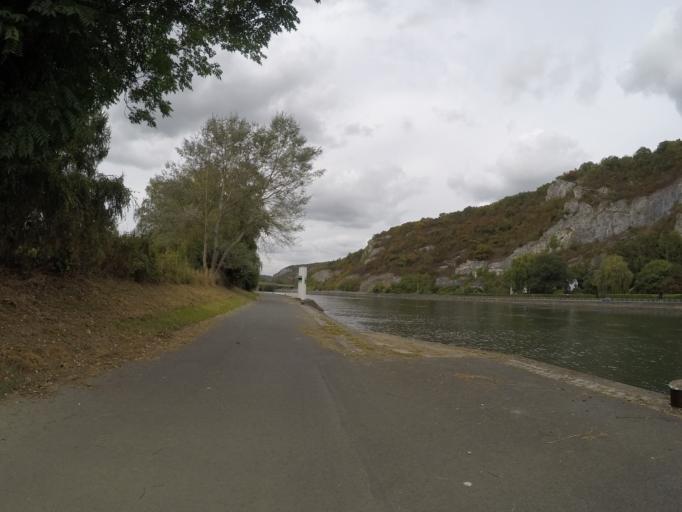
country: BE
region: Wallonia
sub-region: Province de Namur
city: Anhee
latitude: 50.3028
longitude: 4.8953
